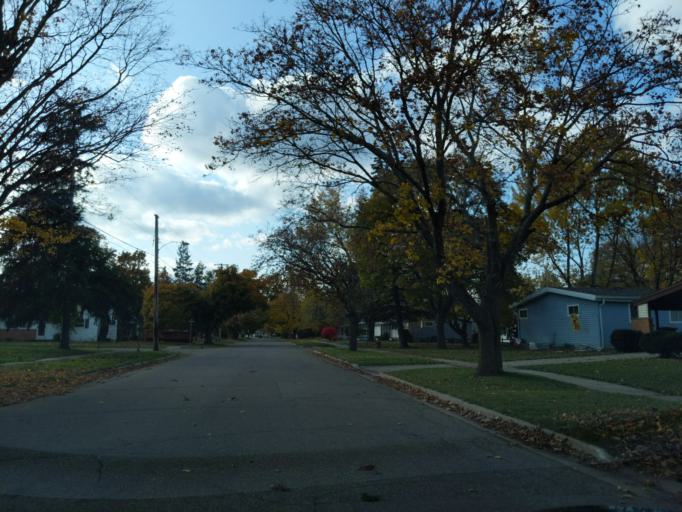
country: US
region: Michigan
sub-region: Ingham County
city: East Lansing
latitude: 42.7484
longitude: -84.5160
